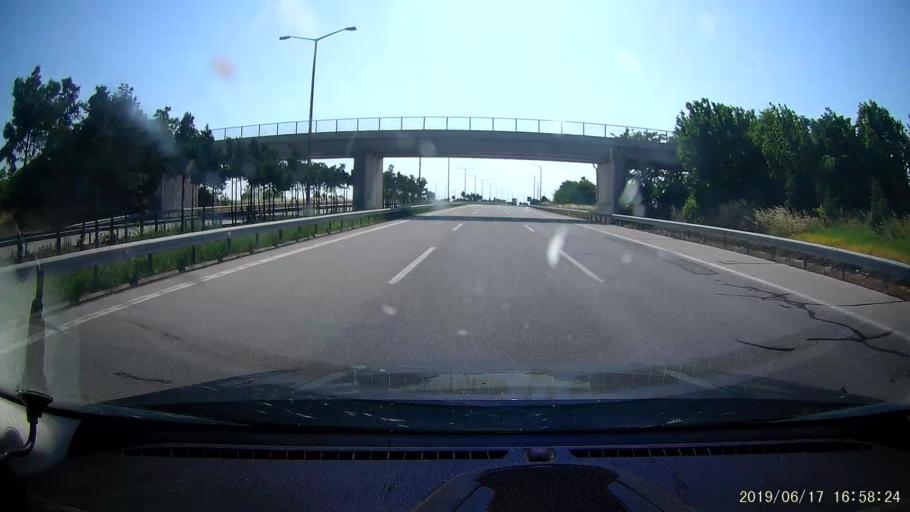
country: TR
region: Edirne
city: Haskoy
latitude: 41.6102
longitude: 26.8893
